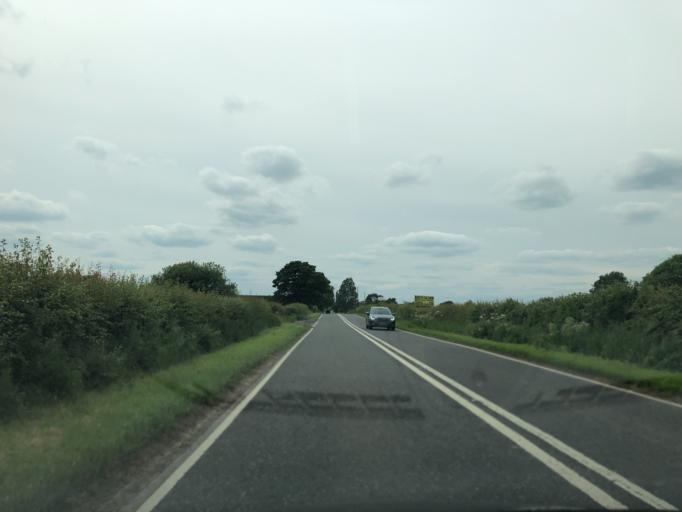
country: GB
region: England
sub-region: North Yorkshire
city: Thirsk
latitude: 54.2315
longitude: -1.2829
